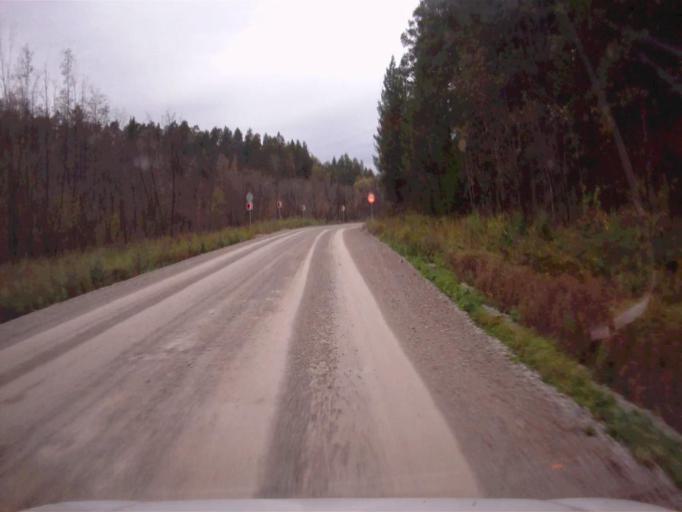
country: RU
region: Chelyabinsk
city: Nyazepetrovsk
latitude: 56.0458
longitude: 59.5036
